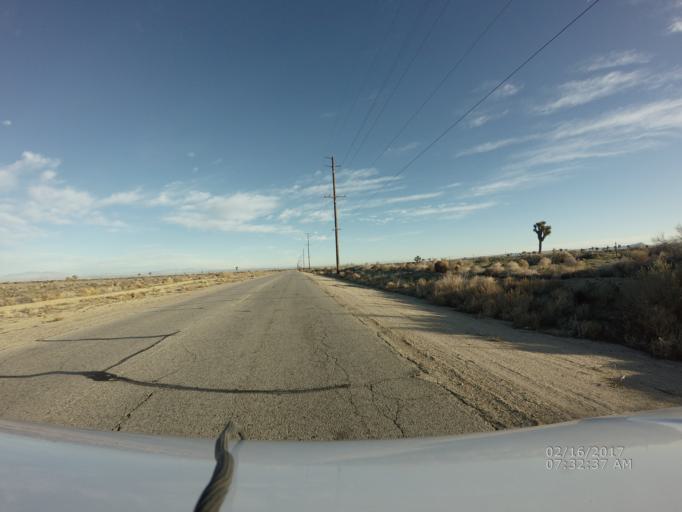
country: US
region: California
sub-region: Los Angeles County
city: Littlerock
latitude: 34.6359
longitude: -117.9697
